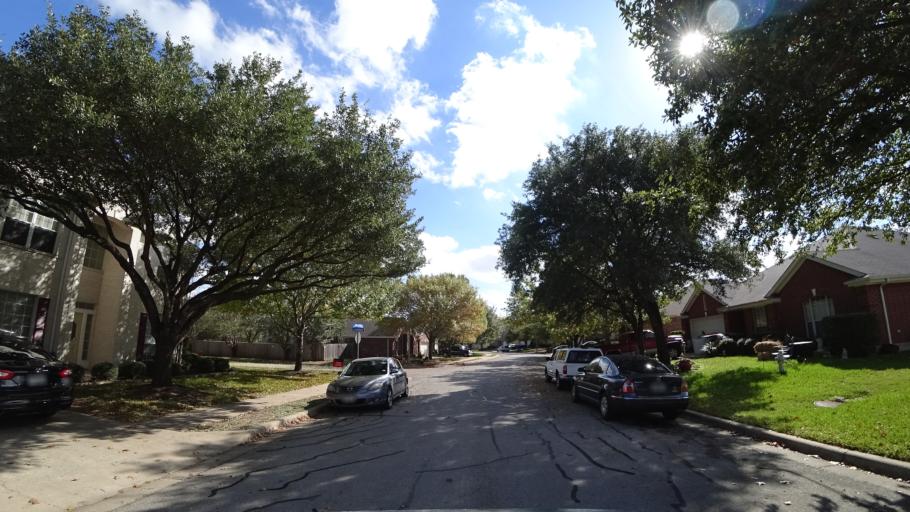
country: US
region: Texas
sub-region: Travis County
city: Windemere
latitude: 30.4595
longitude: -97.6564
